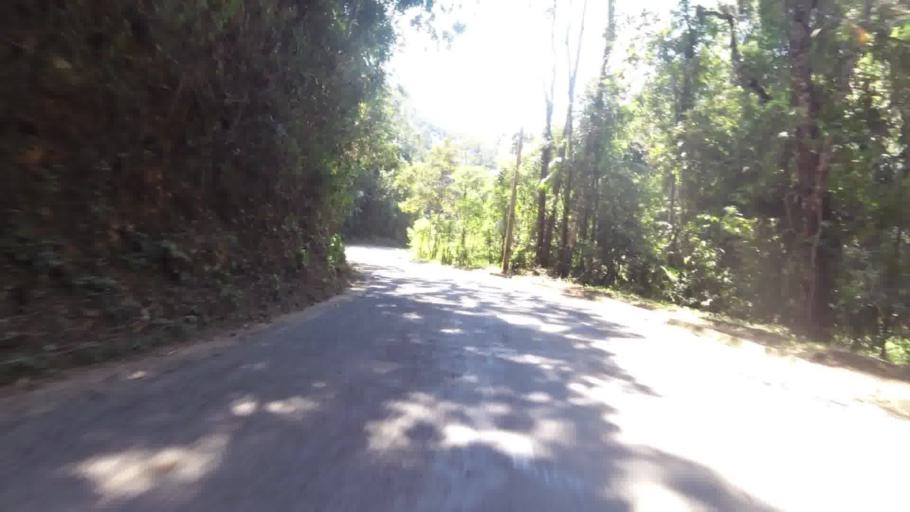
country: BR
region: Espirito Santo
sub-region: Marechal Floriano
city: Marechal Floriano
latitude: -20.4499
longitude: -40.8916
